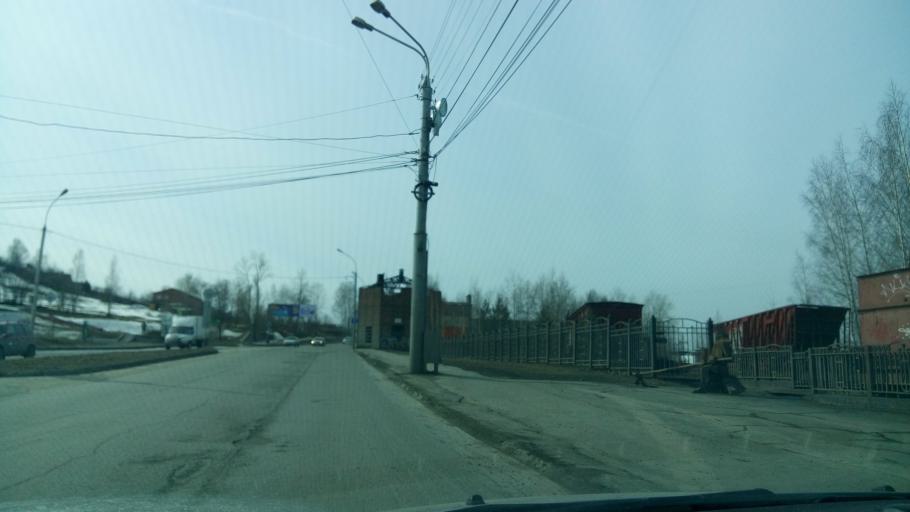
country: RU
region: Sverdlovsk
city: Nizhniy Tagil
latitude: 57.9034
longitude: 59.9478
